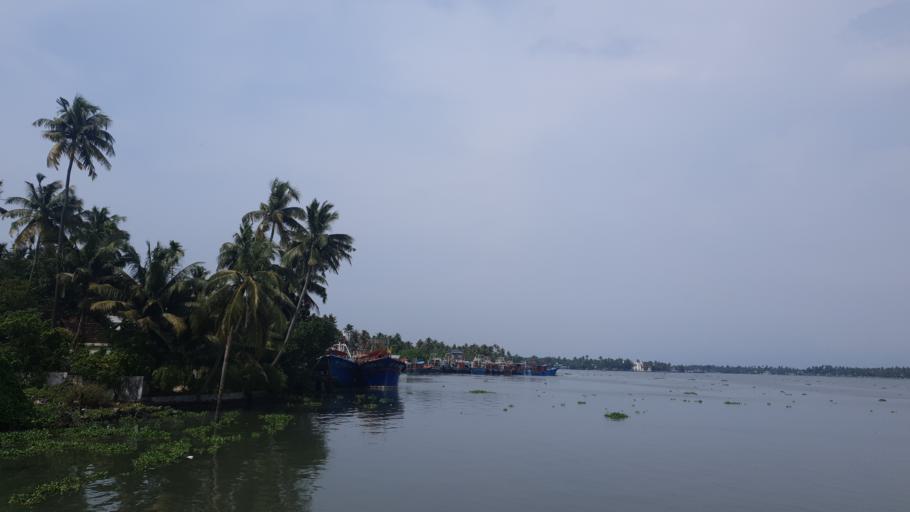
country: IN
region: Kerala
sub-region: Ernakulam
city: Cochin
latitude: 9.9892
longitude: 76.2402
